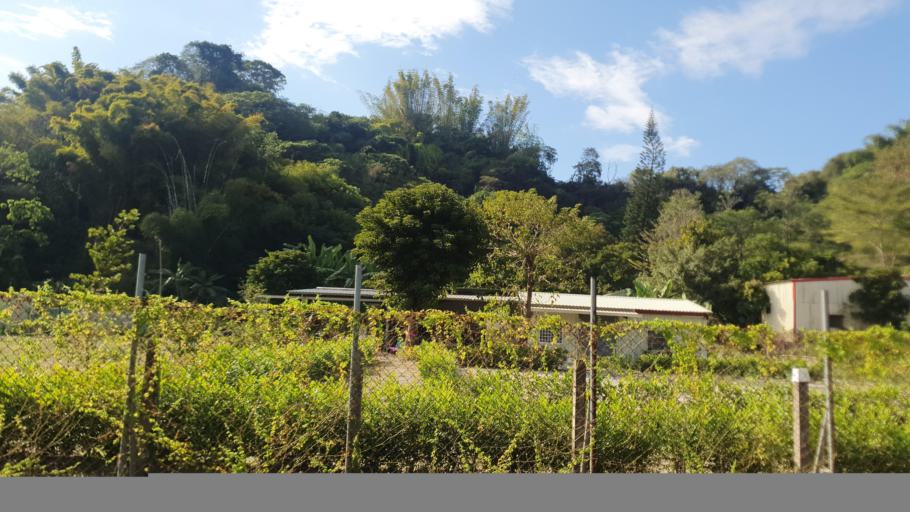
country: TW
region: Taiwan
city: Yujing
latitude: 23.0192
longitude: 120.3975
